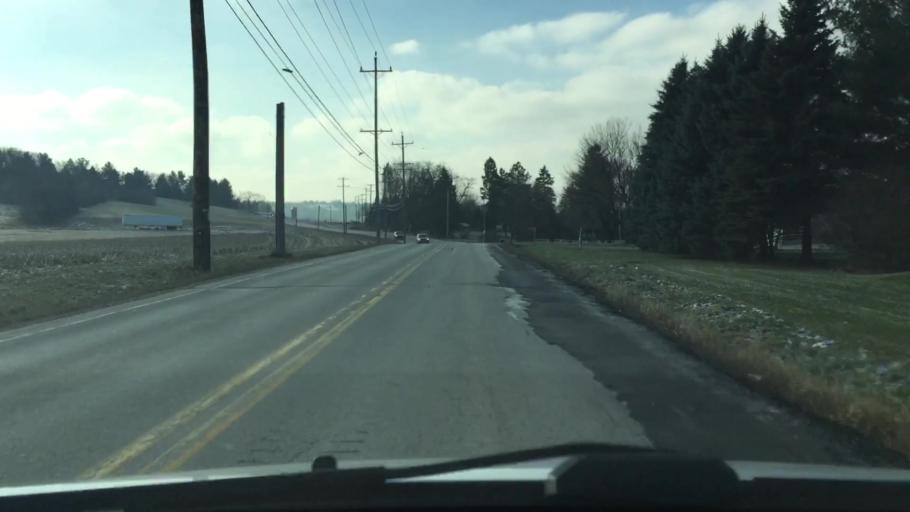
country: US
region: Wisconsin
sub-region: Waukesha County
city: Waukesha
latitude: 43.0082
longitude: -88.2885
